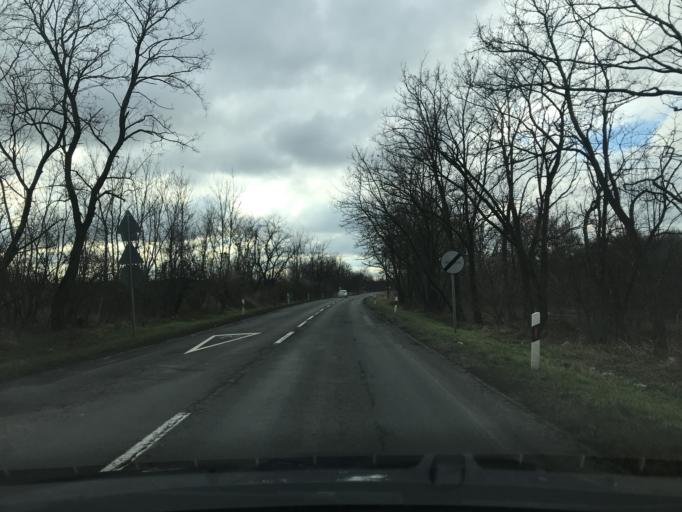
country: HU
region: Bacs-Kiskun
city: Hajos
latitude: 46.3558
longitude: 19.1131
